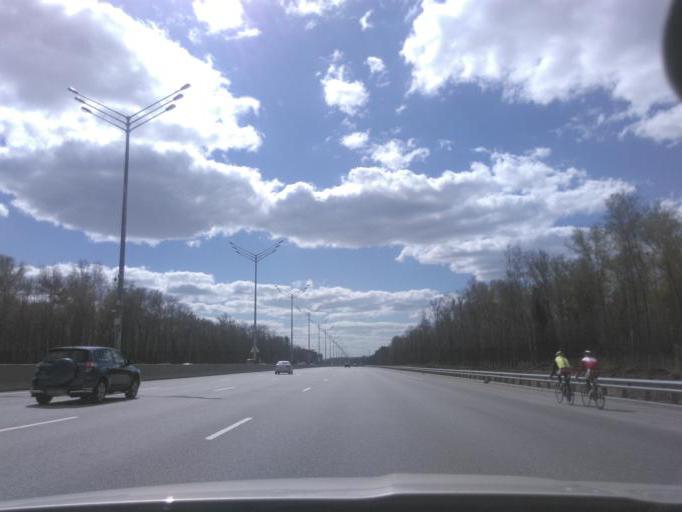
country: RU
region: Moscow
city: Khimki
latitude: 55.9307
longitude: 37.4523
